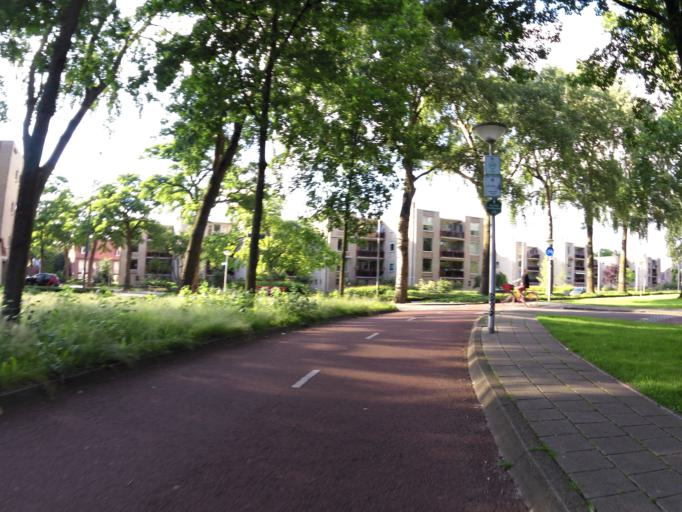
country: NL
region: North Brabant
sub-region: Gemeente Eindhoven
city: Eindhoven
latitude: 51.4260
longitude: 5.4717
